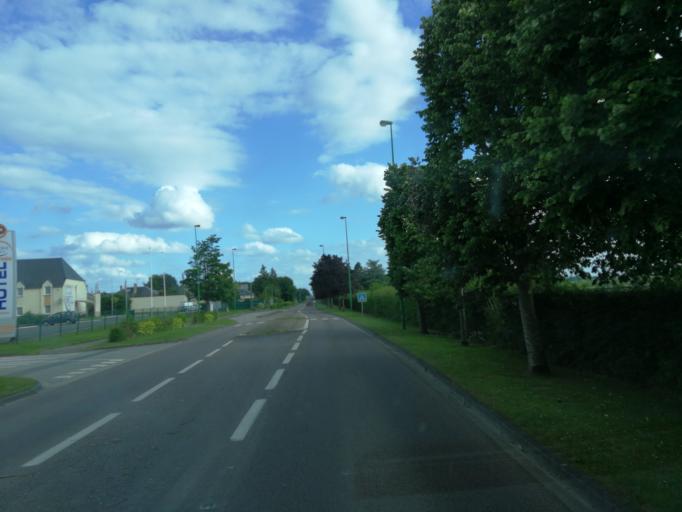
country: FR
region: Haute-Normandie
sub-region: Departement de l'Eure
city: Le Neubourg
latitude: 49.1387
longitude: 0.9042
